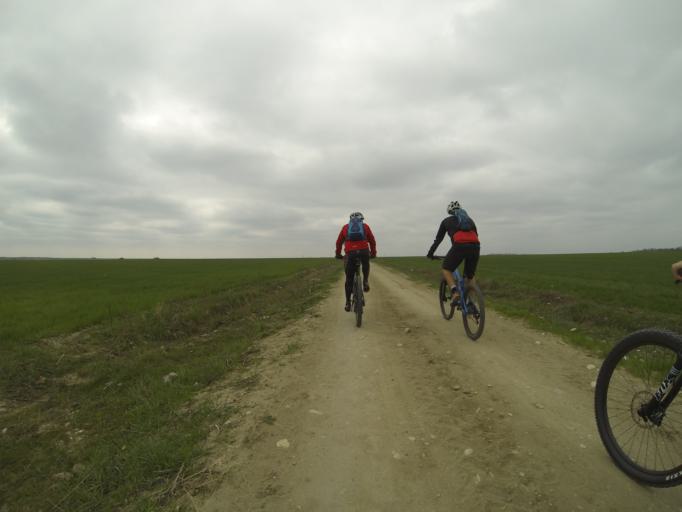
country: RO
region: Dolj
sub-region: Comuna Predesti
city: Predesti
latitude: 44.3378
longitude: 23.6264
